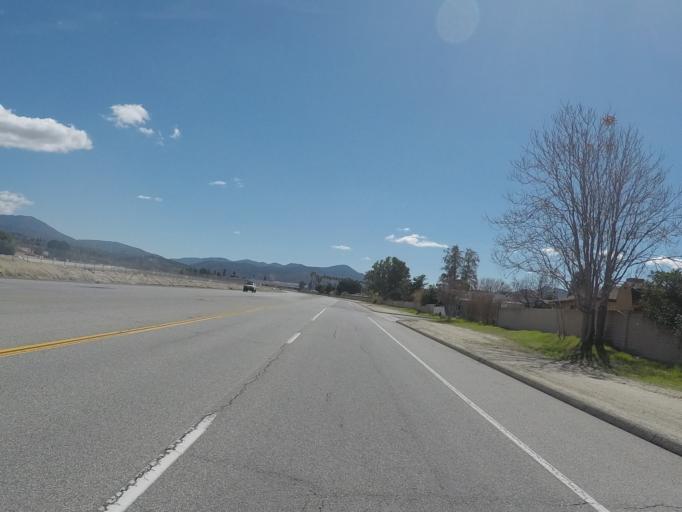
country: US
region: California
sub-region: Riverside County
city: Valle Vista
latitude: 33.7558
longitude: -116.9081
